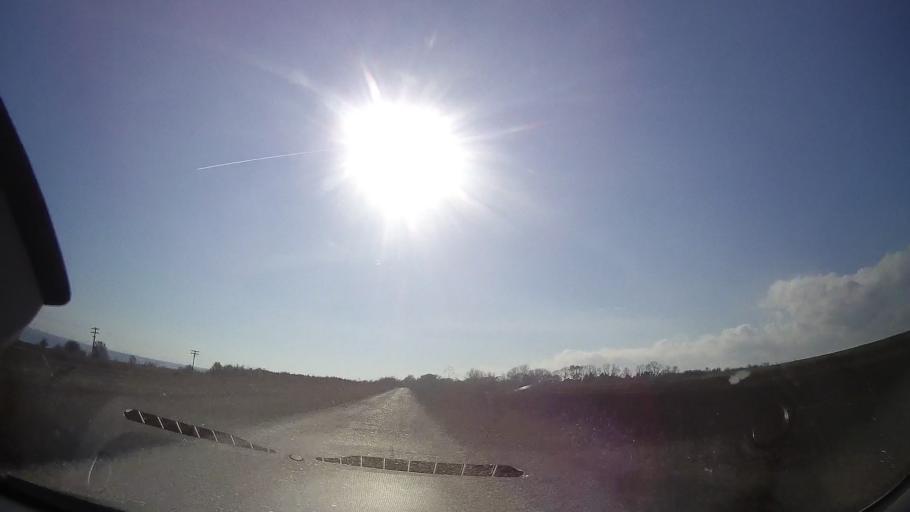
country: RO
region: Constanta
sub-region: Comuna Douazeci si Trei August
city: Douazeci si Trei August
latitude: 43.9063
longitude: 28.6191
